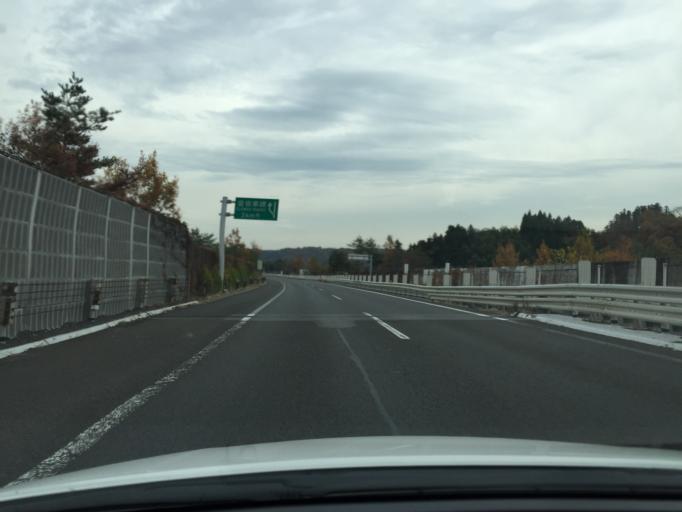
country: JP
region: Fukushima
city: Fukushima-shi
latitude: 37.7202
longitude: 140.4314
